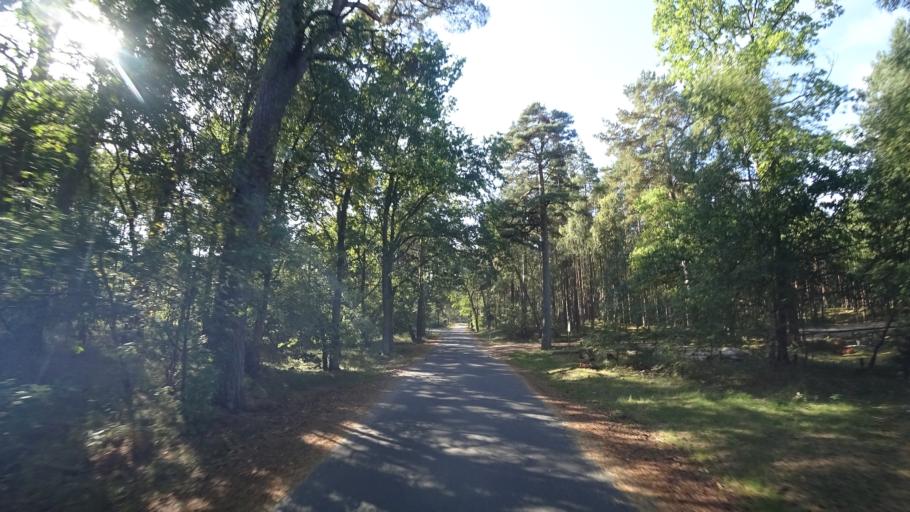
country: SE
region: Skane
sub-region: Kristianstads Kommun
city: Ahus
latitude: 55.9189
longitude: 14.3199
